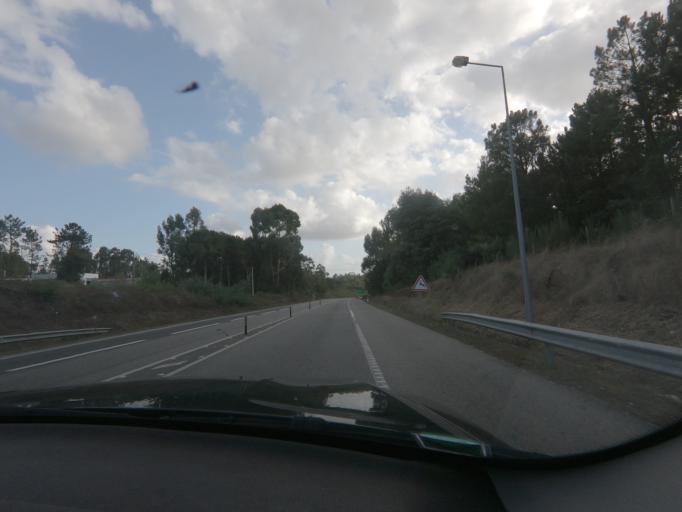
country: PT
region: Viseu
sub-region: Concelho de Tondela
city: Tondela
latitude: 40.5840
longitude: -8.0176
